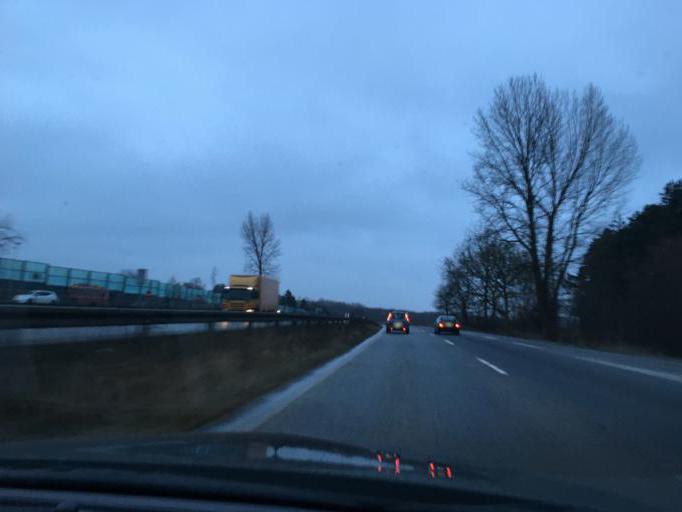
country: DK
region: Capital Region
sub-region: Horsholm Kommune
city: Horsholm
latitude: 55.8649
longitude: 12.4856
